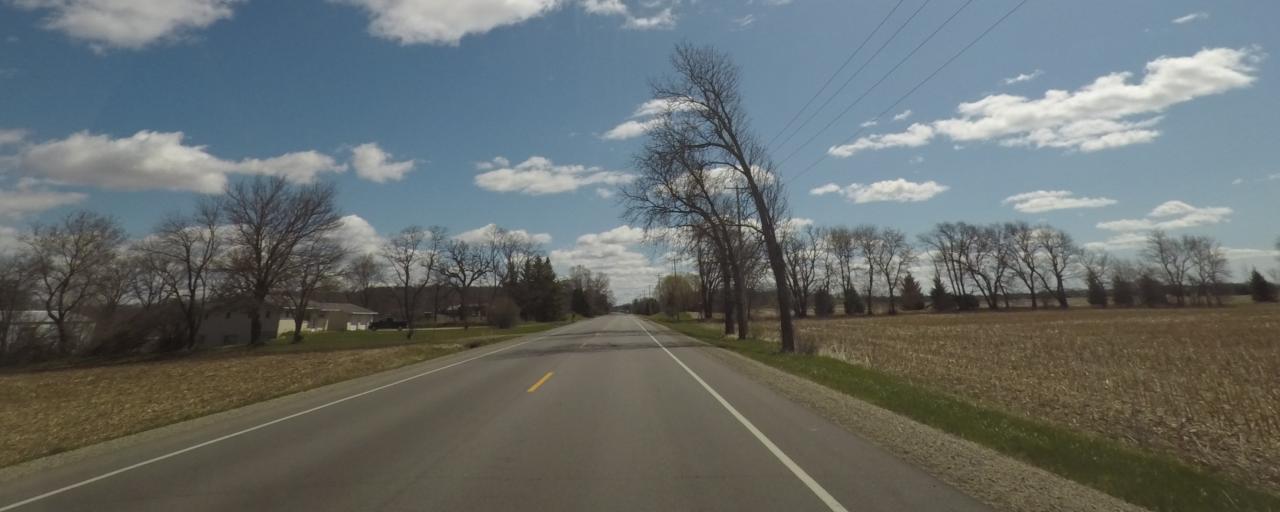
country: US
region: Wisconsin
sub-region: Jefferson County
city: Lake Mills
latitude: 43.0885
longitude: -88.9696
